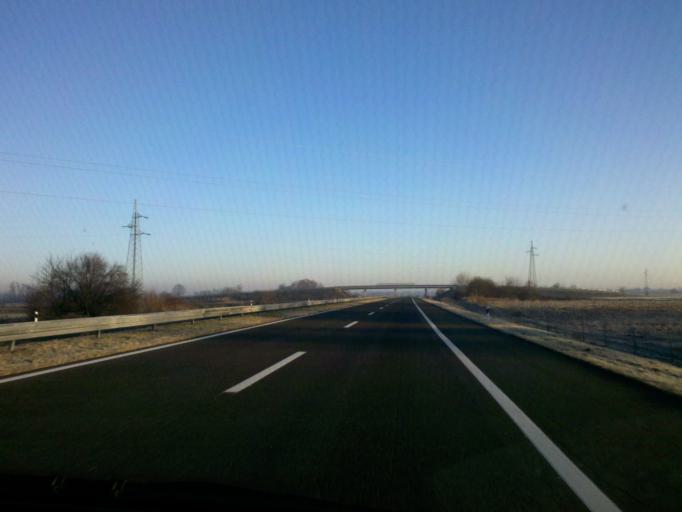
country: HR
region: Medimurska
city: Orehovica
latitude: 46.3229
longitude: 16.5161
